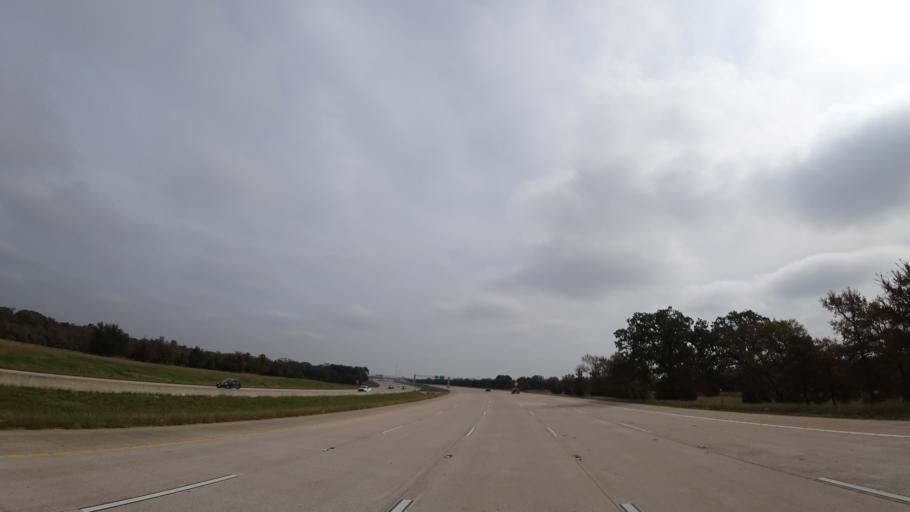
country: US
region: Texas
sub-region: Williamson County
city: Brushy Creek
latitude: 30.4775
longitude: -97.7291
